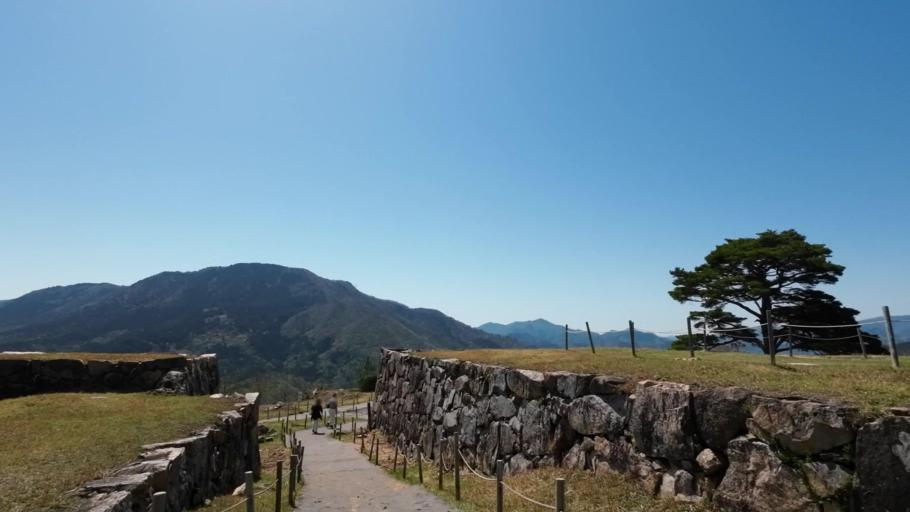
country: JP
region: Hyogo
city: Toyooka
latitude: 35.2999
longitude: 134.8291
